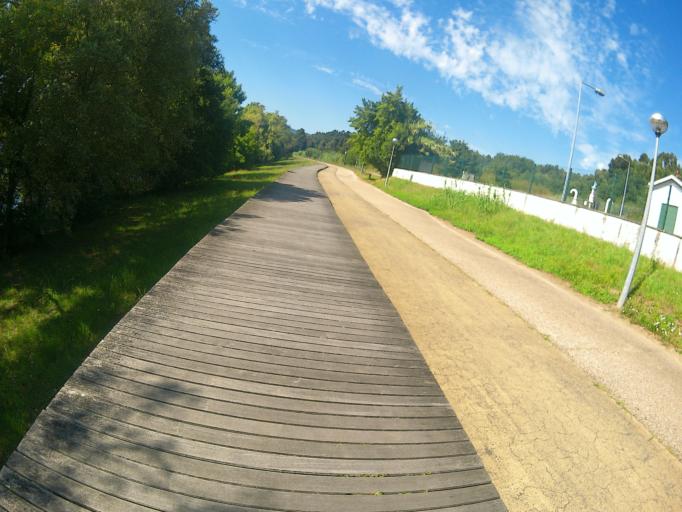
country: PT
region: Viana do Castelo
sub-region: Valenca
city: Valenca
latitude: 42.0208
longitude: -8.6560
